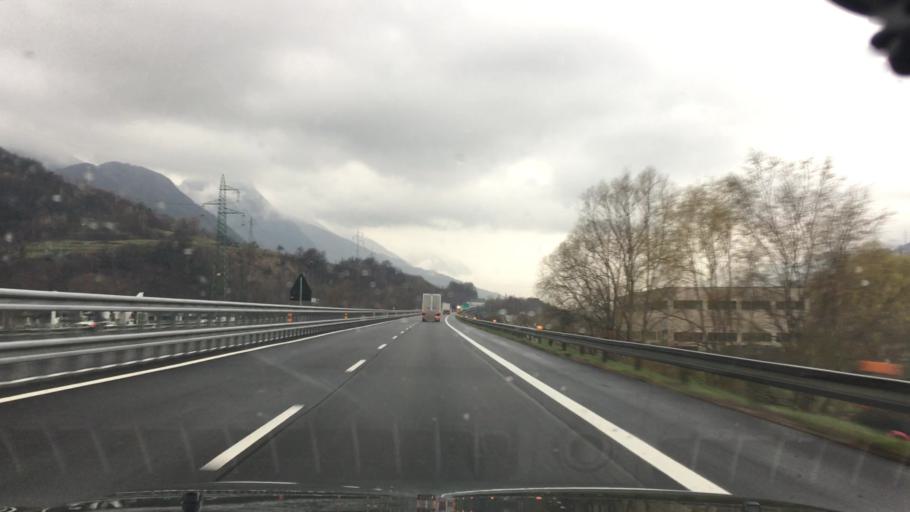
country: IT
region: Aosta Valley
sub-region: Valle d'Aosta
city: Chambave
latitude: 45.7435
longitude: 7.5577
